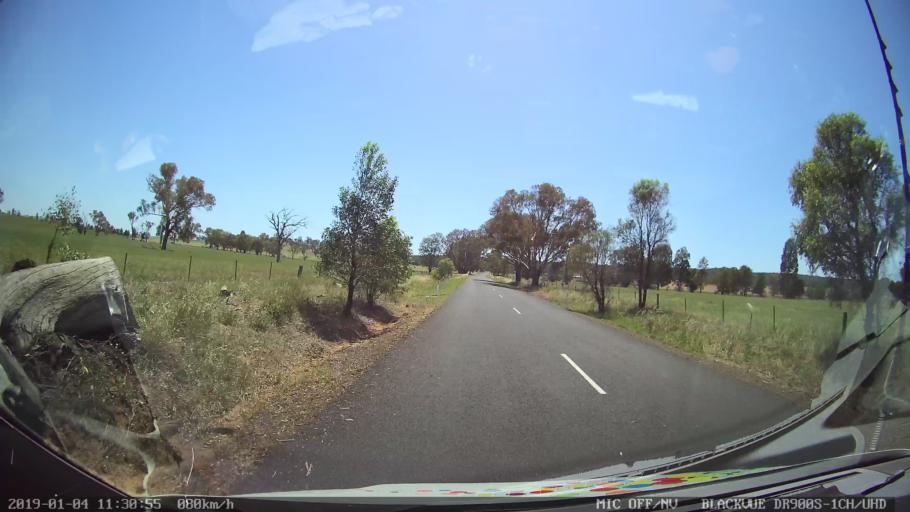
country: AU
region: New South Wales
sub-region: Cabonne
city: Molong
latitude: -33.0748
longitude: 148.7868
